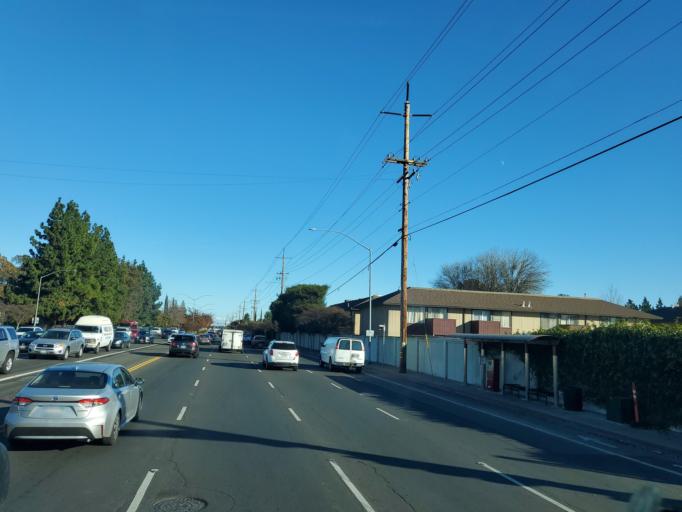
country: US
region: California
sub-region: San Joaquin County
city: Lincoln Village
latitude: 38.0209
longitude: -121.3150
